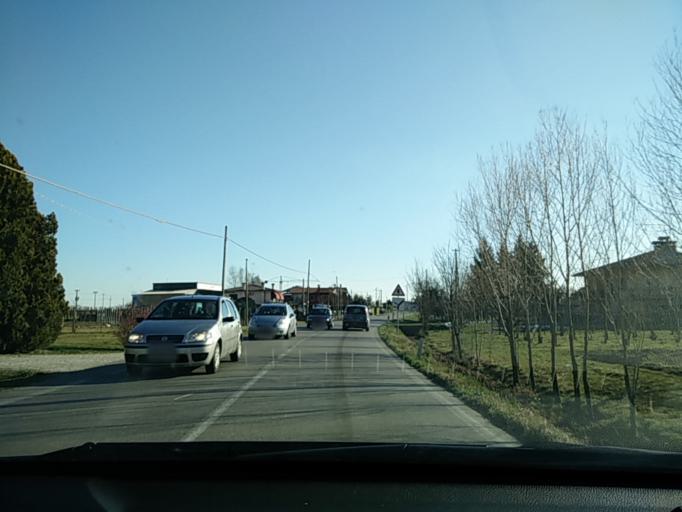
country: IT
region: Veneto
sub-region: Provincia di Treviso
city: Fontanelle
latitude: 45.8402
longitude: 12.4789
